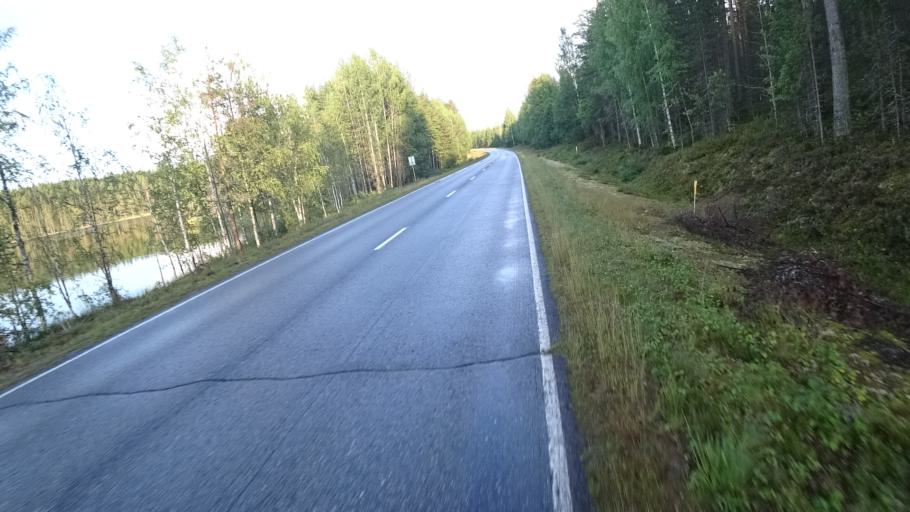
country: FI
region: North Karelia
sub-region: Joensuu
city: Ilomantsi
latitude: 62.6247
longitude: 31.1131
